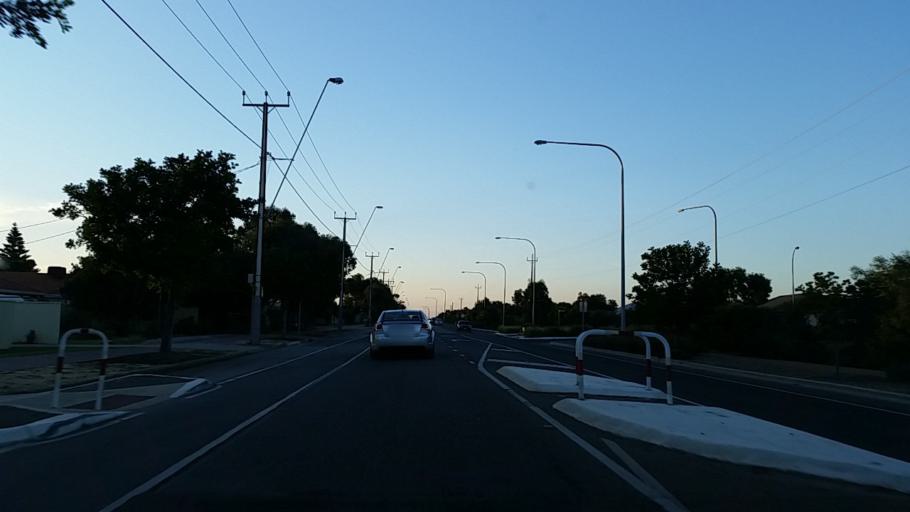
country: AU
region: South Australia
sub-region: Onkaparinga
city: Seaford
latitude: -35.1768
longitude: 138.4764
